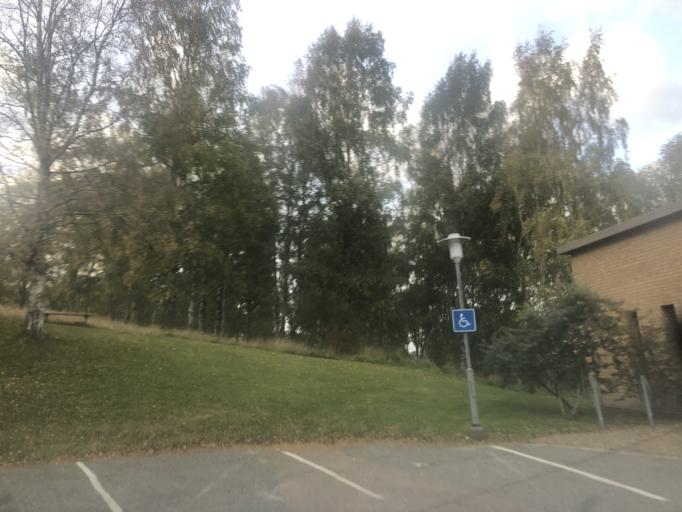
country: SE
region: Vaestra Goetaland
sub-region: Goteborg
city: Majorna
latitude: 57.6367
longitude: 11.9394
